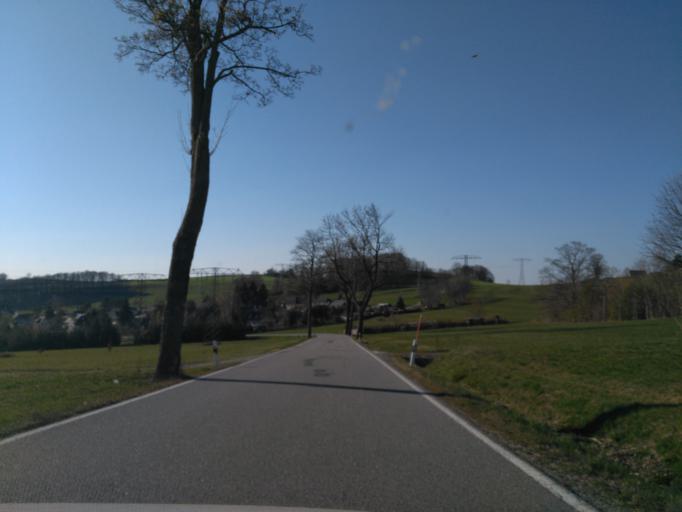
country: DE
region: Saxony
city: Scheibenberg
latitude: 50.5349
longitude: 12.9071
